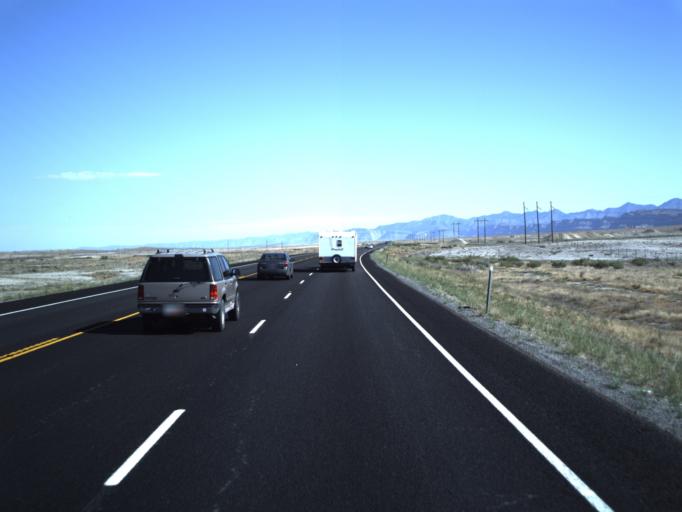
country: US
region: Utah
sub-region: Carbon County
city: East Carbon City
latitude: 39.1555
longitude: -110.3380
